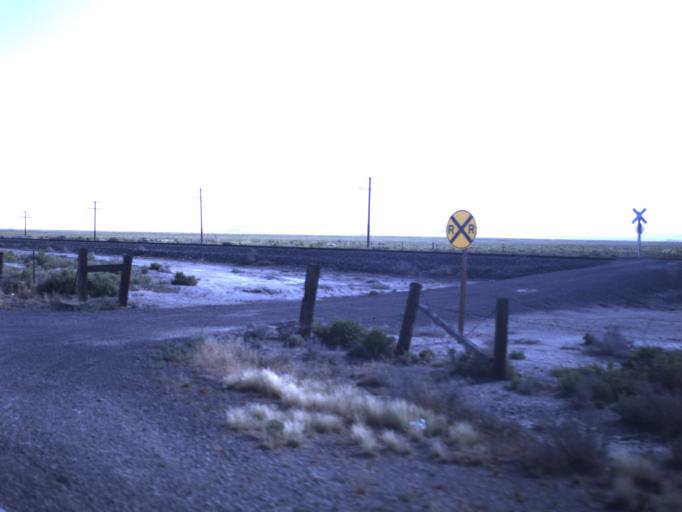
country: US
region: Utah
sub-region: Beaver County
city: Milford
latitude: 38.6095
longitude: -112.9861
